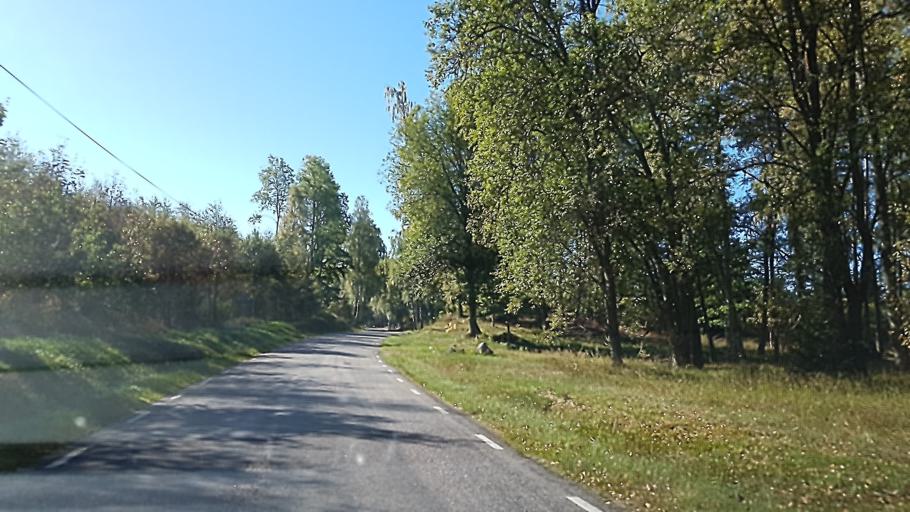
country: SE
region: Kronoberg
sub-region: Ljungby Kommun
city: Ljungby
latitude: 56.8025
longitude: 14.0334
